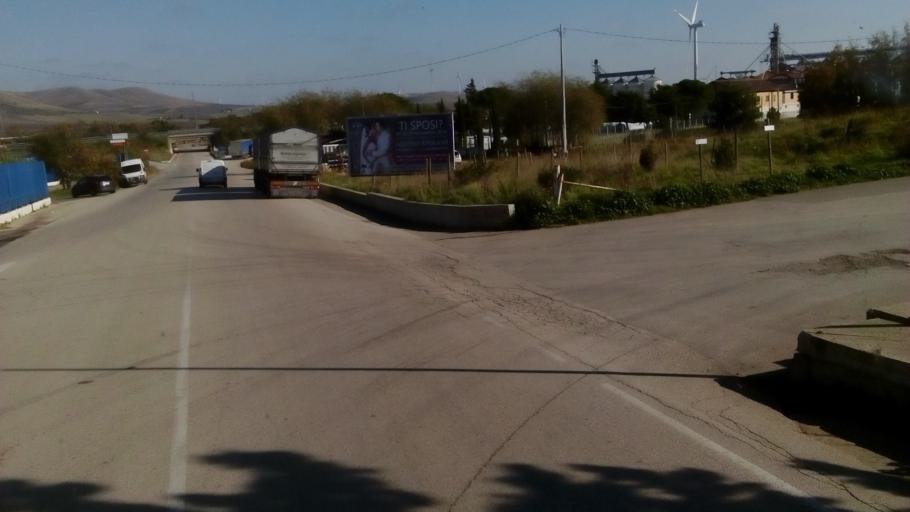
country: IT
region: Apulia
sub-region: Provincia di Foggia
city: Candela
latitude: 41.1502
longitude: 15.5268
